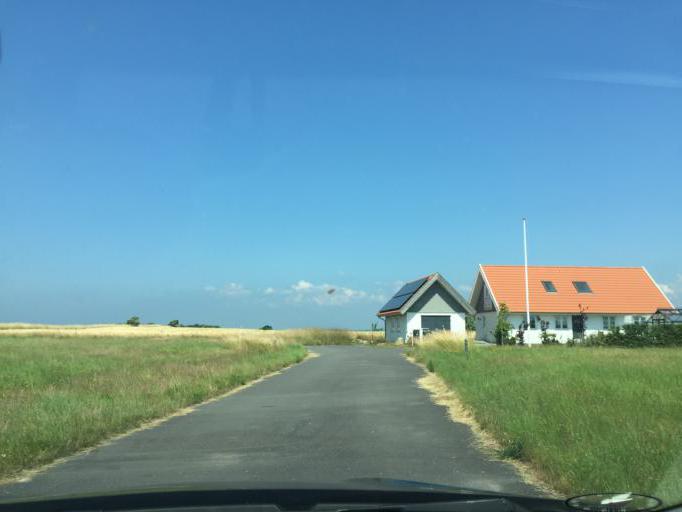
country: DK
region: Zealand
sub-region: Slagelse Kommune
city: Skaelskor
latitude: 55.2141
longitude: 11.1920
